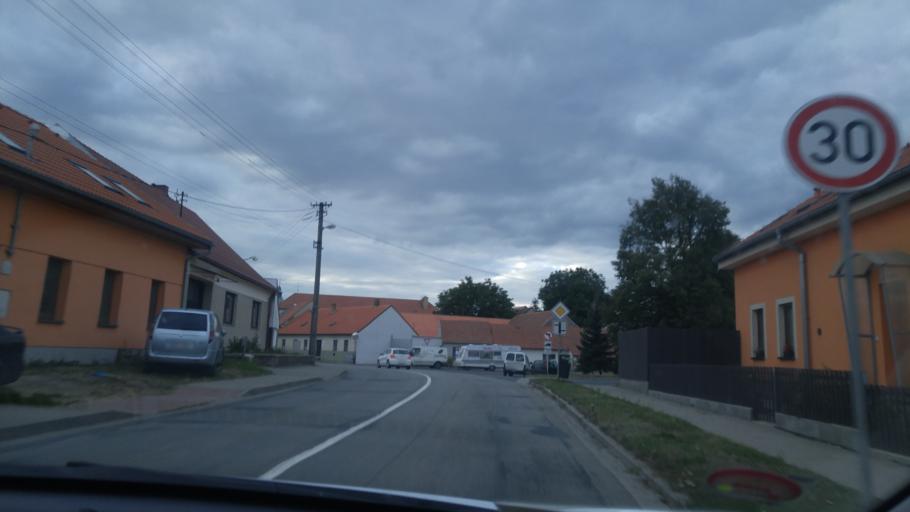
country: CZ
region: South Moravian
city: Ricany
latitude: 49.2096
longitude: 16.4122
